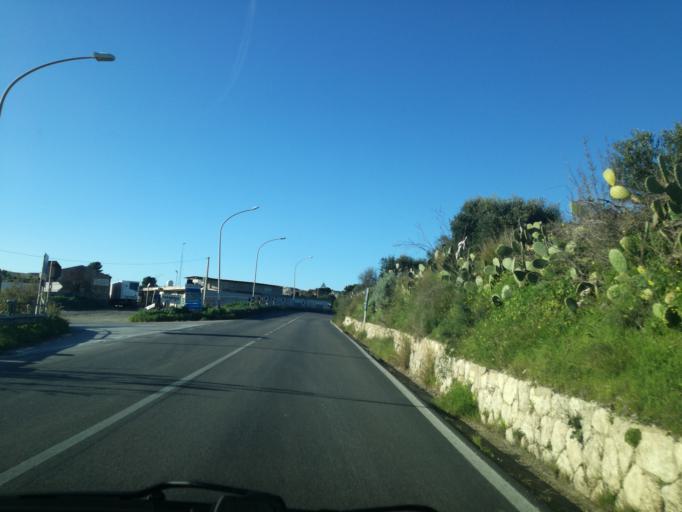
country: IT
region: Sicily
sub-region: Provincia di Caltanissetta
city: Gela
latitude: 37.1013
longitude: 14.1582
